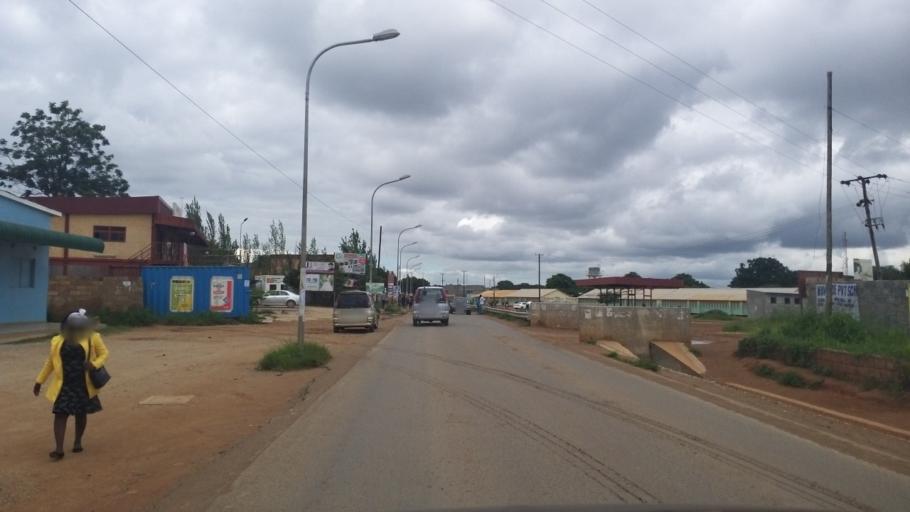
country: ZM
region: Lusaka
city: Lusaka
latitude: -15.4425
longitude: 28.3086
